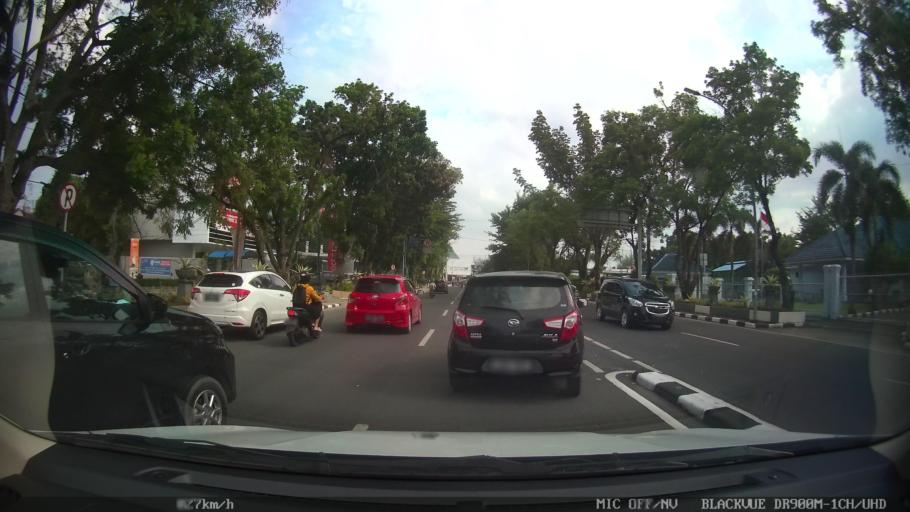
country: ID
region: North Sumatra
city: Medan
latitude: 3.5712
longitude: 98.6780
